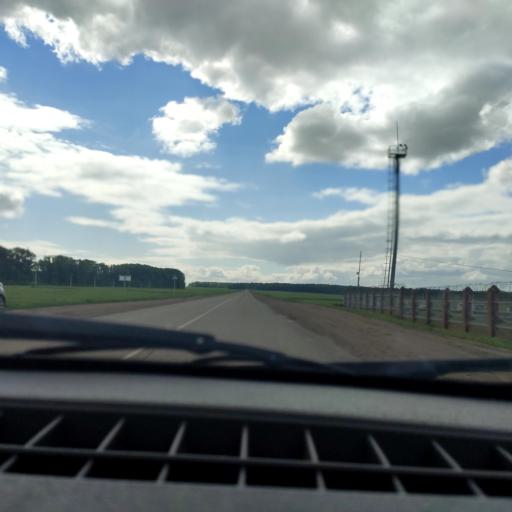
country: RU
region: Bashkortostan
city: Mikhaylovka
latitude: 54.8243
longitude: 55.7630
